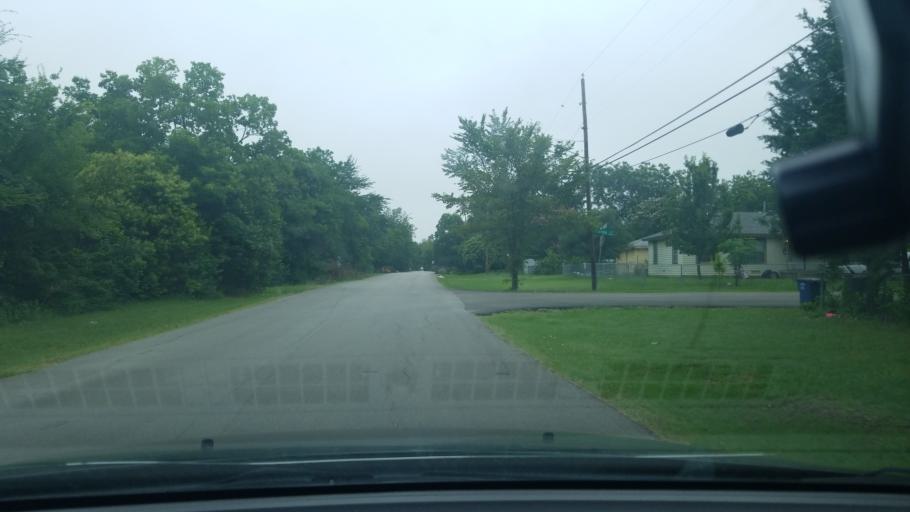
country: US
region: Texas
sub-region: Dallas County
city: Balch Springs
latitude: 32.7576
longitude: -96.6772
